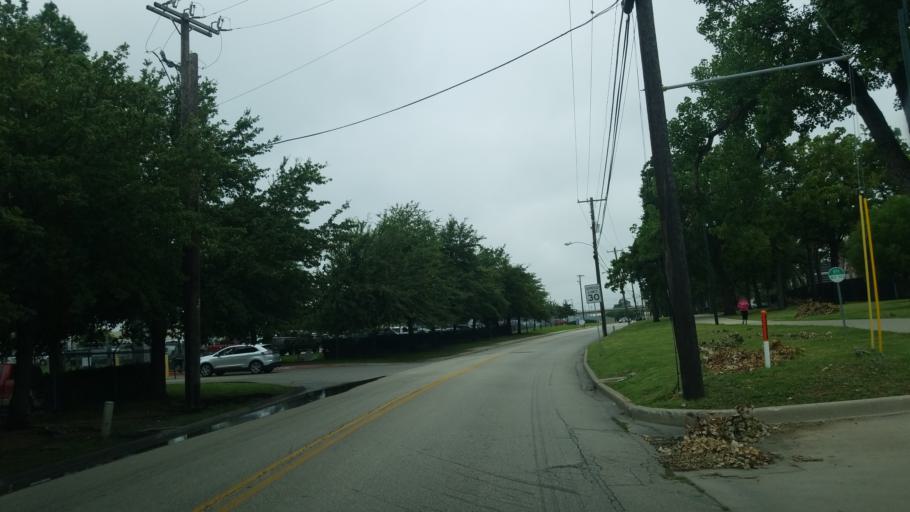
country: US
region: Texas
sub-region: Dallas County
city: University Park
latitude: 32.8489
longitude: -96.8659
